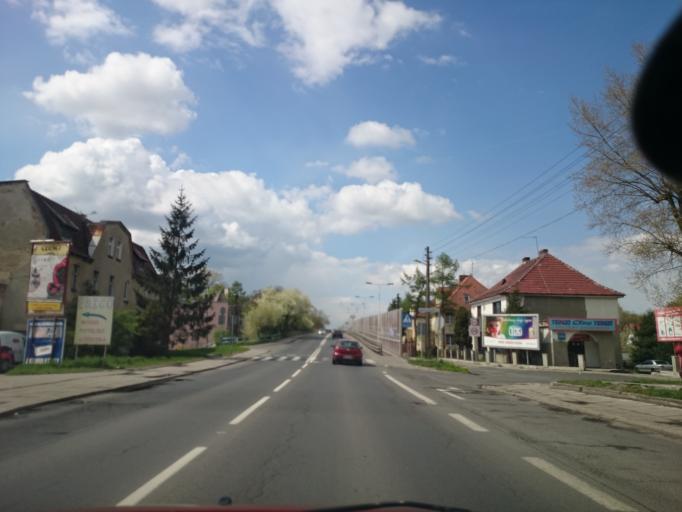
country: PL
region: Opole Voivodeship
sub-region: Powiat opolski
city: Opole
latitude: 50.6559
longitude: 17.9515
